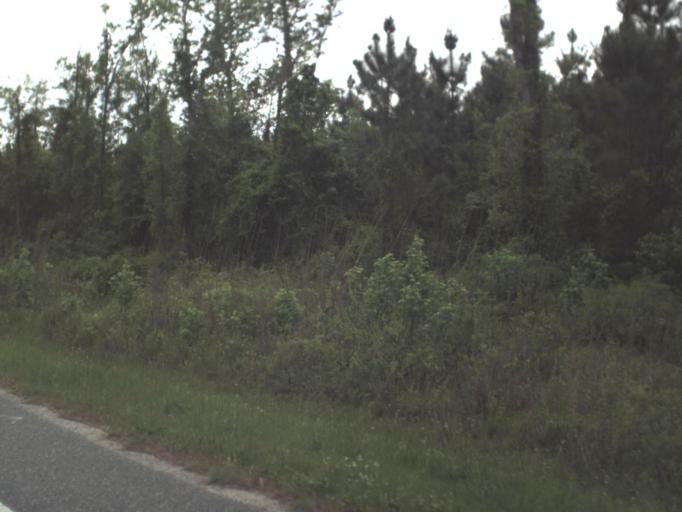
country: US
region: Alabama
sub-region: Escambia County
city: East Brewton
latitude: 30.9039
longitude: -87.0362
